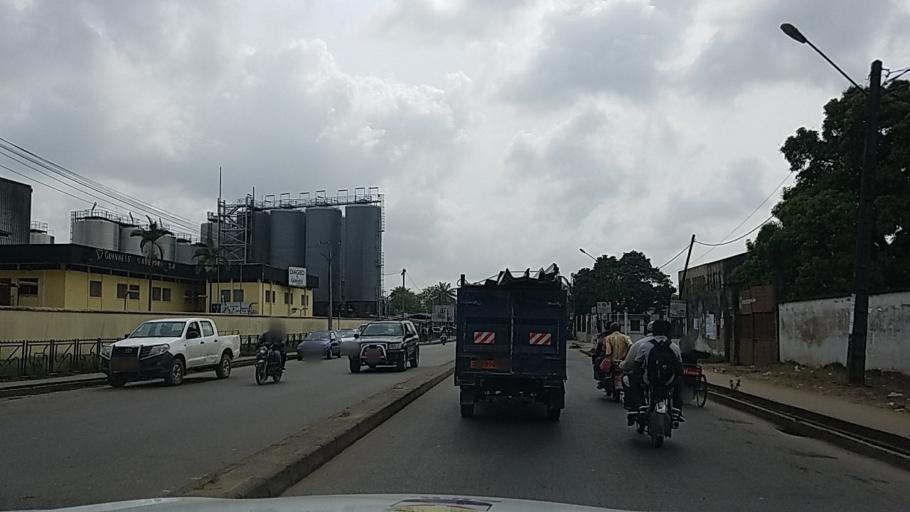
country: CM
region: Littoral
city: Douala
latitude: 4.0475
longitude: 9.7422
